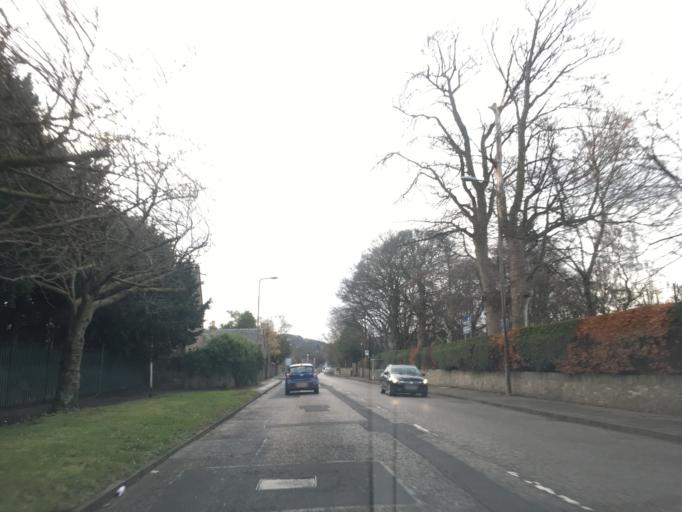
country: GB
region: Scotland
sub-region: Edinburgh
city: Colinton
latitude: 55.9107
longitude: -3.2490
